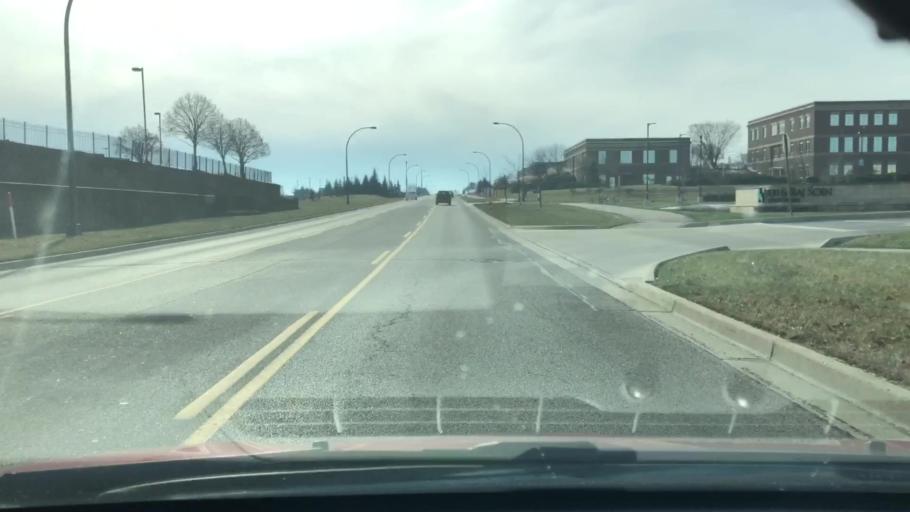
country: US
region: Ohio
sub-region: Greene County
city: Wright-Patterson AFB
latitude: 39.7702
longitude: -84.0595
